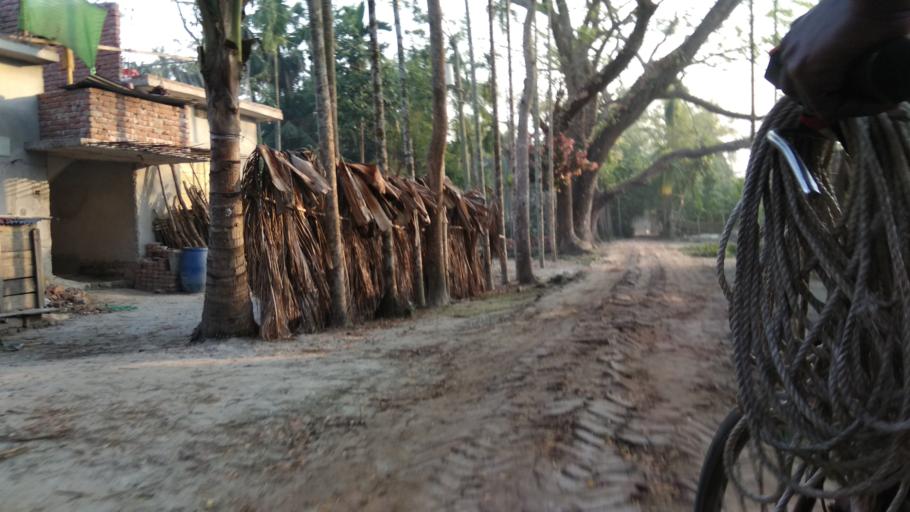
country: BD
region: Barisal
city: Mehendiganj
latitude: 22.9305
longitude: 90.4104
